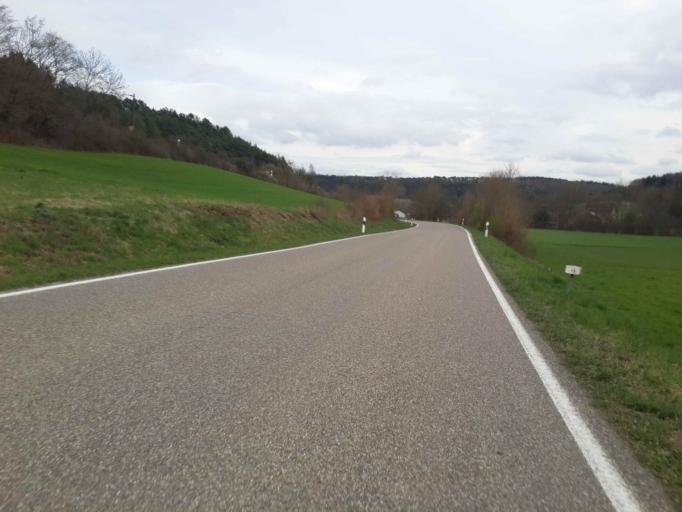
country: DE
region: Baden-Wuerttemberg
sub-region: Regierungsbezirk Stuttgart
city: Boxberg
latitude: 49.4908
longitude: 9.6115
